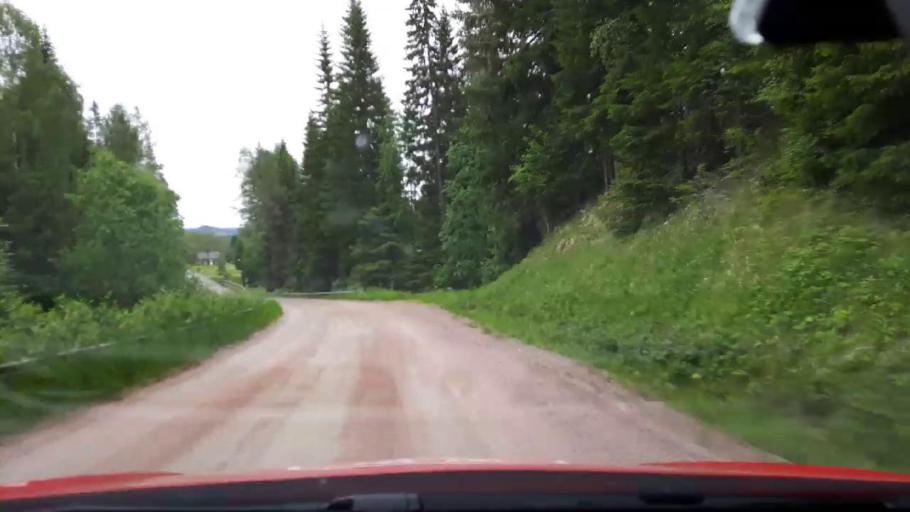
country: SE
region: Jaemtland
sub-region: Ragunda Kommun
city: Hammarstrand
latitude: 63.2099
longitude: 16.1049
